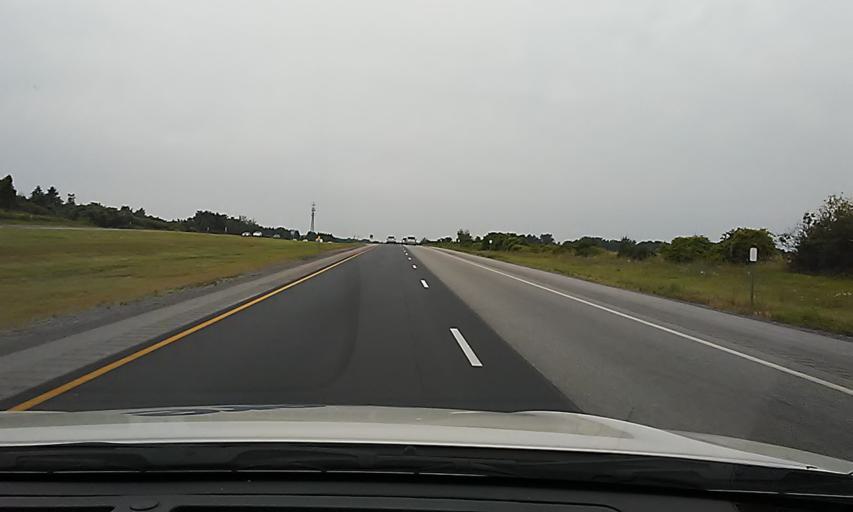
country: US
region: New York
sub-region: Genesee County
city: Batavia
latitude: 43.0171
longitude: -78.0857
